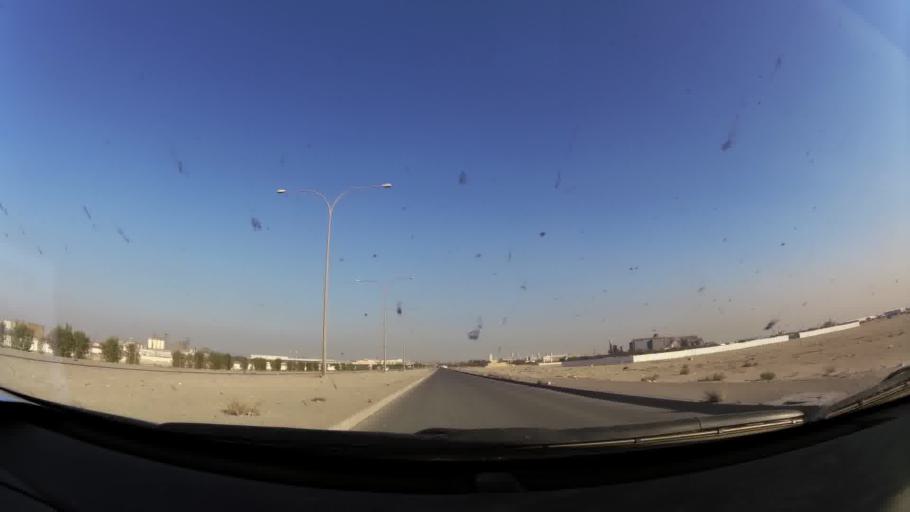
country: KW
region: Al Ahmadi
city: Al Ahmadi
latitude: 28.9953
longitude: 48.1167
